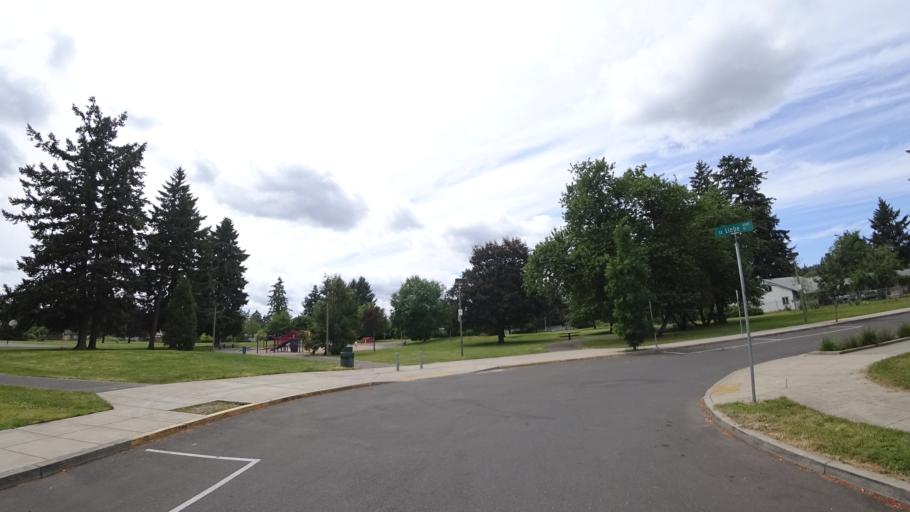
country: US
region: Oregon
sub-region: Multnomah County
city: Lents
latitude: 45.4868
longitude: -122.5419
